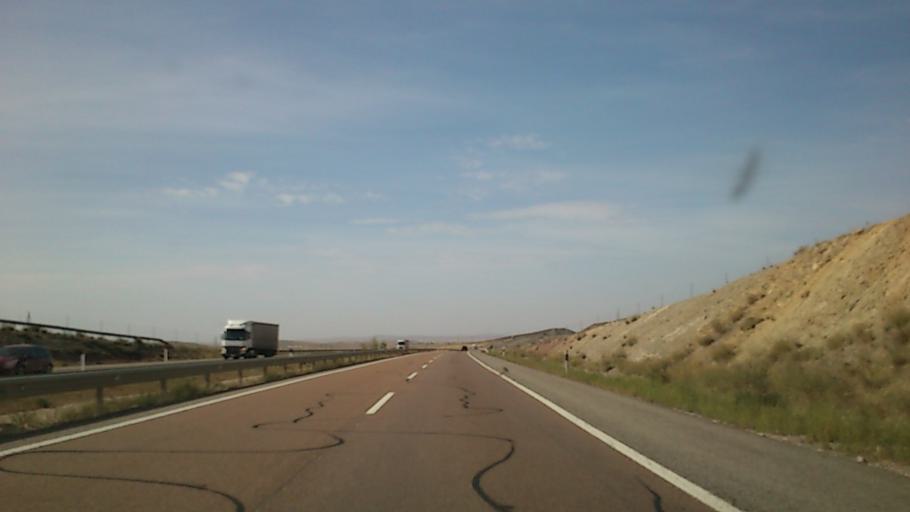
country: ES
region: Aragon
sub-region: Provincia de Teruel
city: Singra
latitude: 40.6410
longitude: -1.3138
